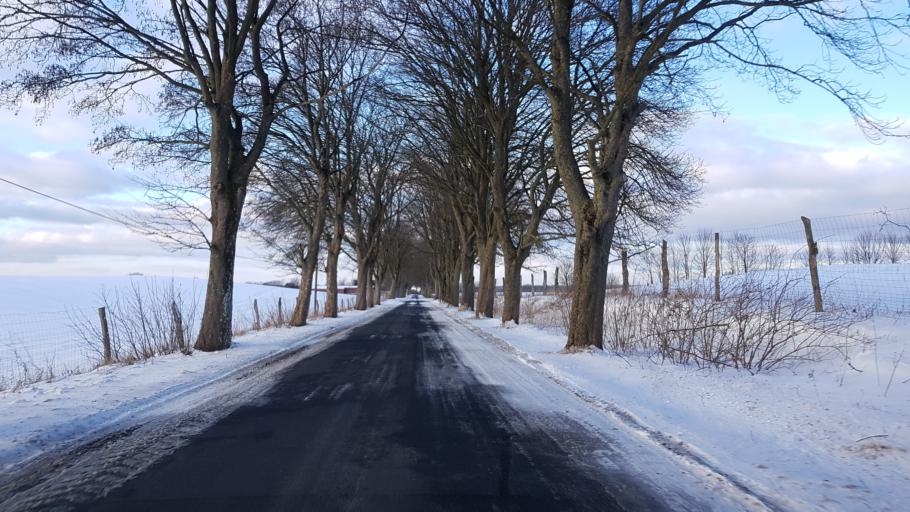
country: PL
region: West Pomeranian Voivodeship
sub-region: Powiat koszalinski
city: Bobolice
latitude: 53.9834
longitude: 16.6891
